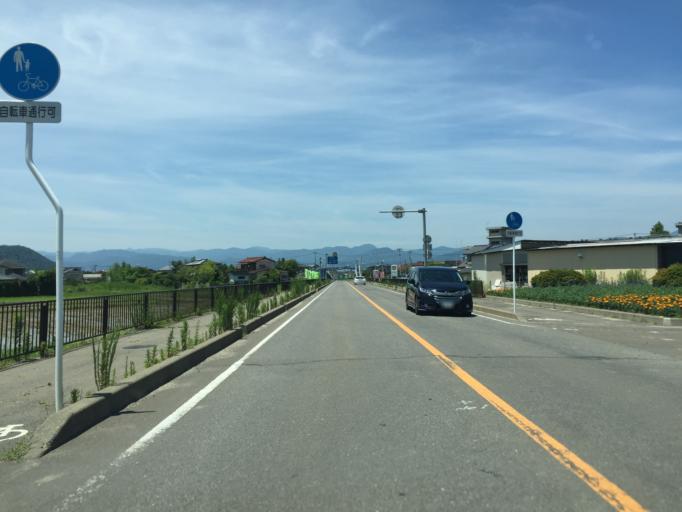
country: JP
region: Fukushima
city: Fukushima-shi
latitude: 37.7695
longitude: 140.5112
